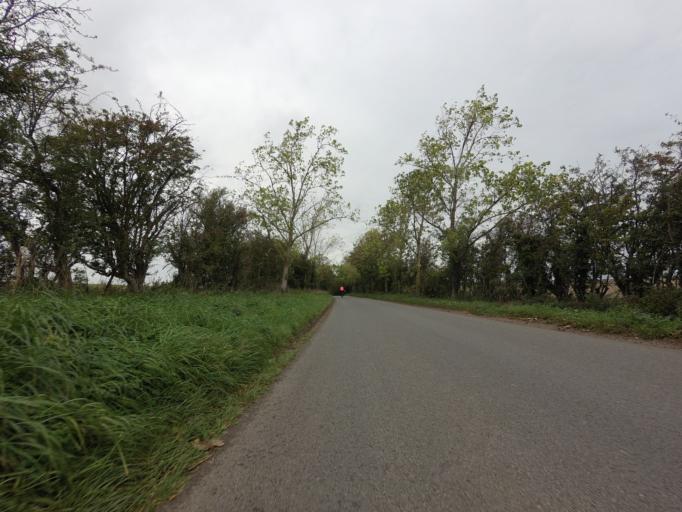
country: GB
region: England
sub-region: Cambridgeshire
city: Duxford
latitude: 52.0446
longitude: 0.1657
